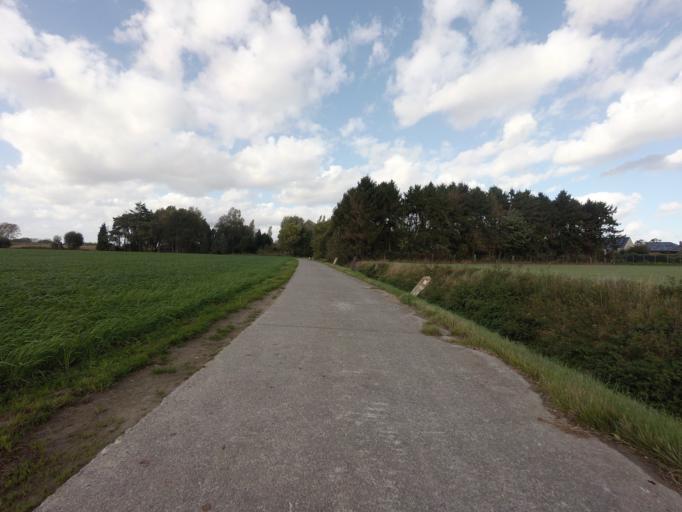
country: BE
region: Flanders
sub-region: Provincie Vlaams-Brabant
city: Zemst
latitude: 50.9885
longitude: 4.4538
